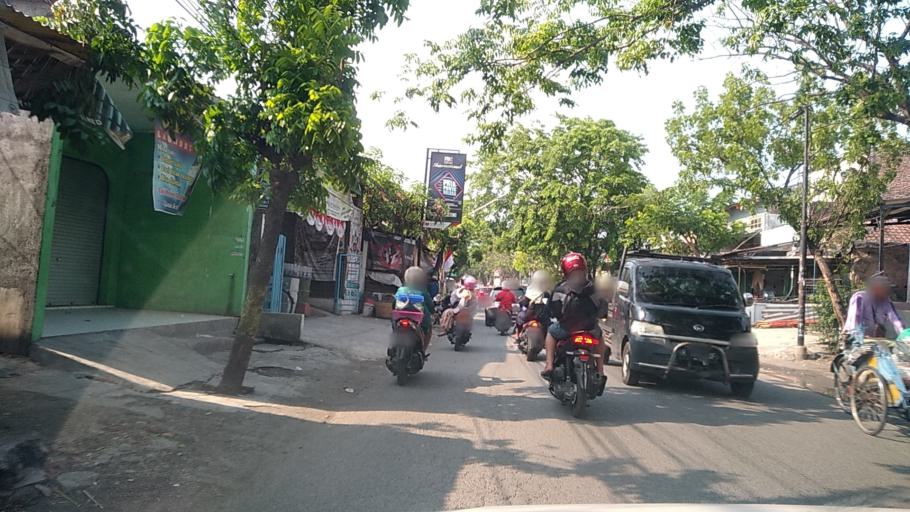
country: ID
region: Central Java
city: Semarang
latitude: -6.9798
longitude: 110.4490
